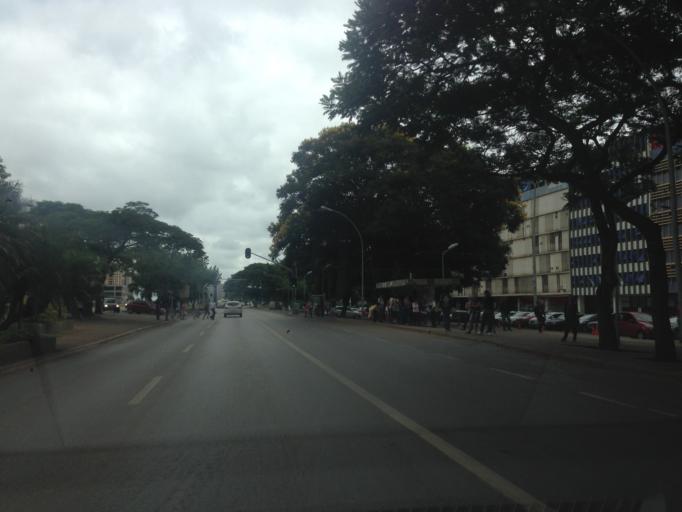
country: BR
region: Federal District
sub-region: Brasilia
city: Brasilia
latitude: -15.7969
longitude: -47.8914
